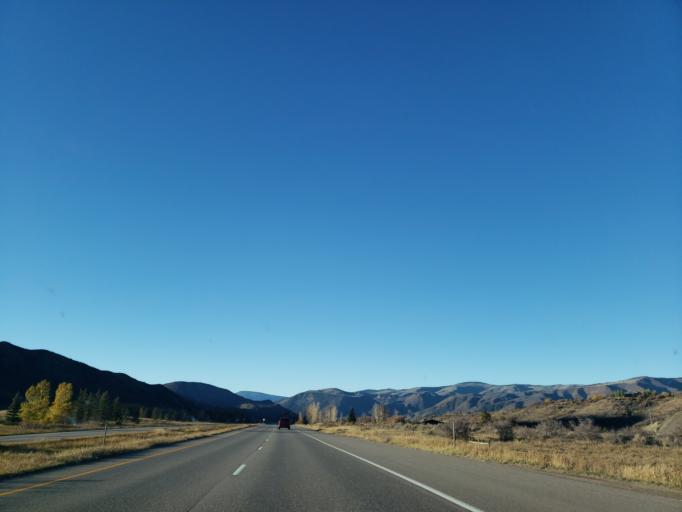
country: US
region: Colorado
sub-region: Pitkin County
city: Aspen
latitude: 39.2291
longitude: -106.8682
